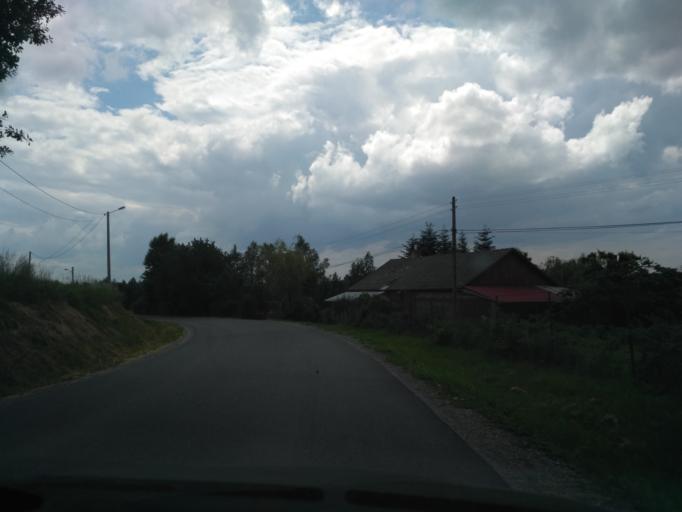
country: PL
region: Subcarpathian Voivodeship
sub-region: Powiat rzeszowski
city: Hyzne
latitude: 49.9350
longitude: 22.1806
